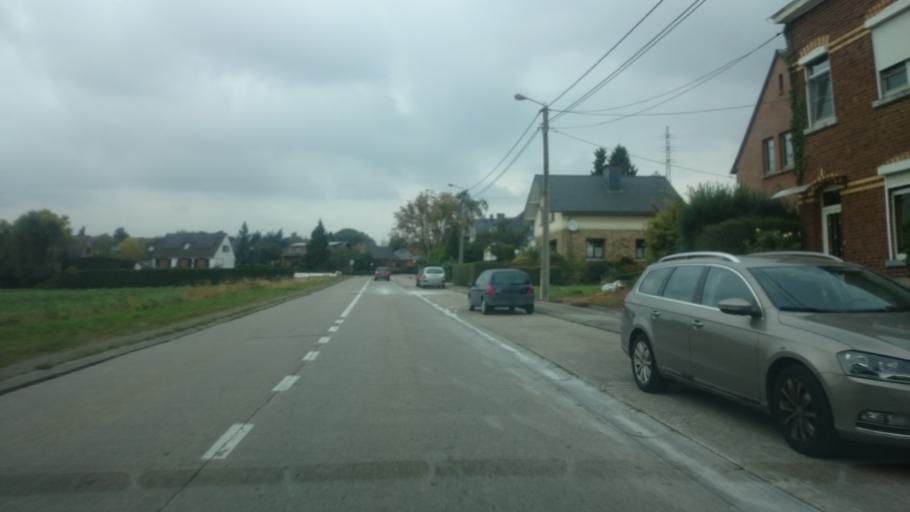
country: BE
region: Wallonia
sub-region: Province de Namur
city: Namur
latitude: 50.4678
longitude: 4.8187
